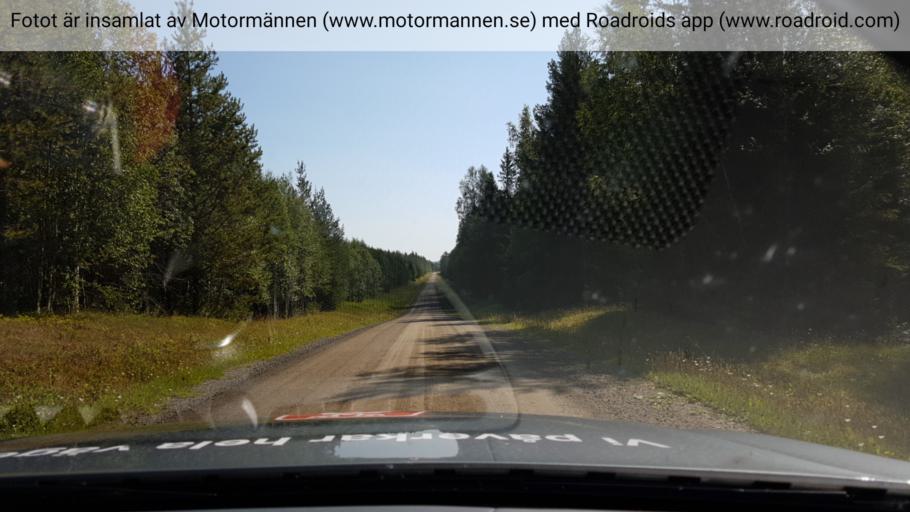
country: SE
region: Jaemtland
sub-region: Stroemsunds Kommun
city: Stroemsund
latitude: 63.3096
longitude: 15.5325
